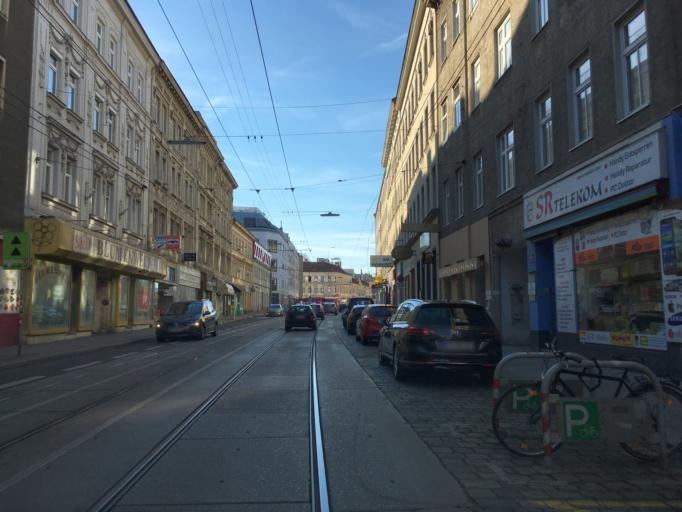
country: AT
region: Vienna
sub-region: Wien Stadt
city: Vienna
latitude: 48.2183
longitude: 16.3300
